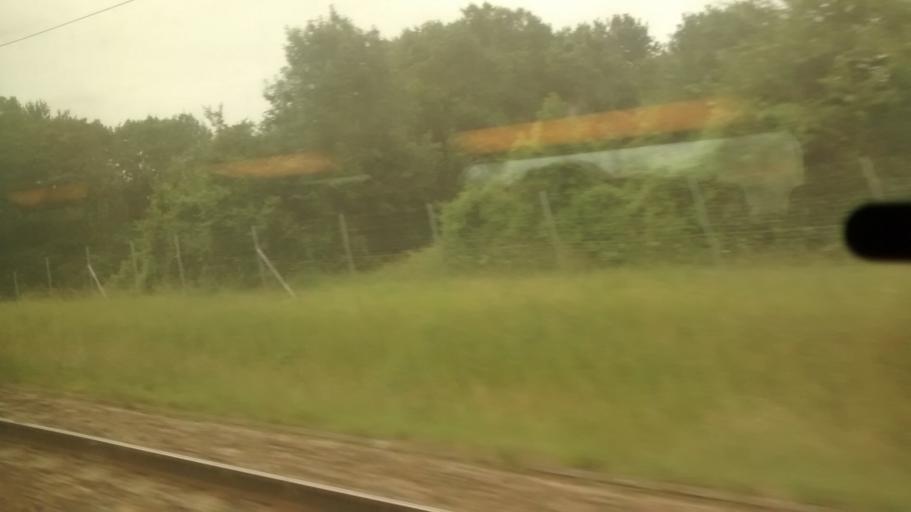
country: FR
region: Ile-de-France
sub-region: Departement de Seine-et-Marne
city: Moisenay
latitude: 48.5539
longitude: 2.7720
